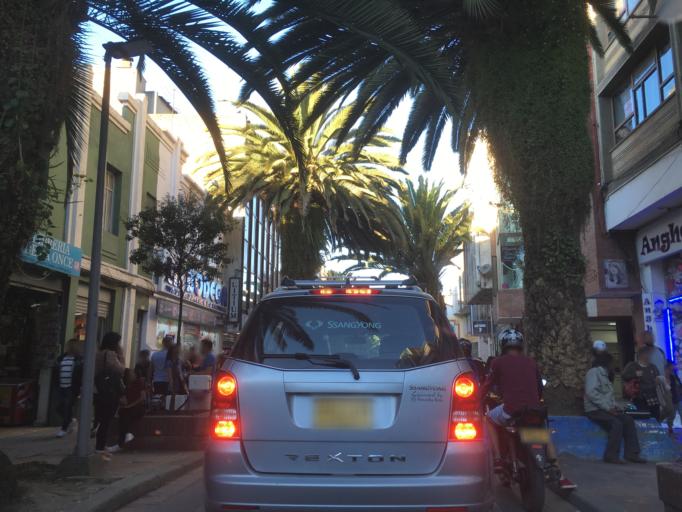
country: CO
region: Boyaca
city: Sogamoso
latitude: 5.7169
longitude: -72.9272
